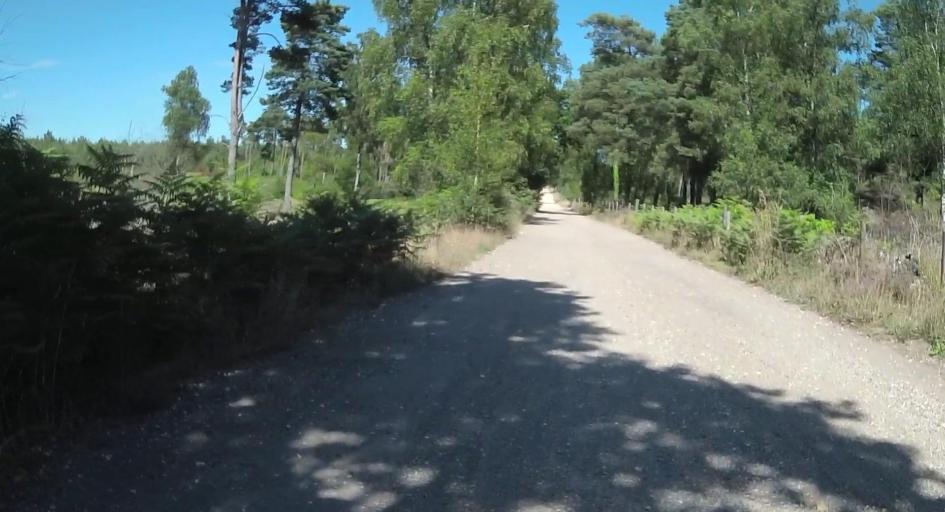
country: GB
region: England
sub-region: Dorset
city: Bovington Camp
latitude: 50.7167
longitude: -2.2605
